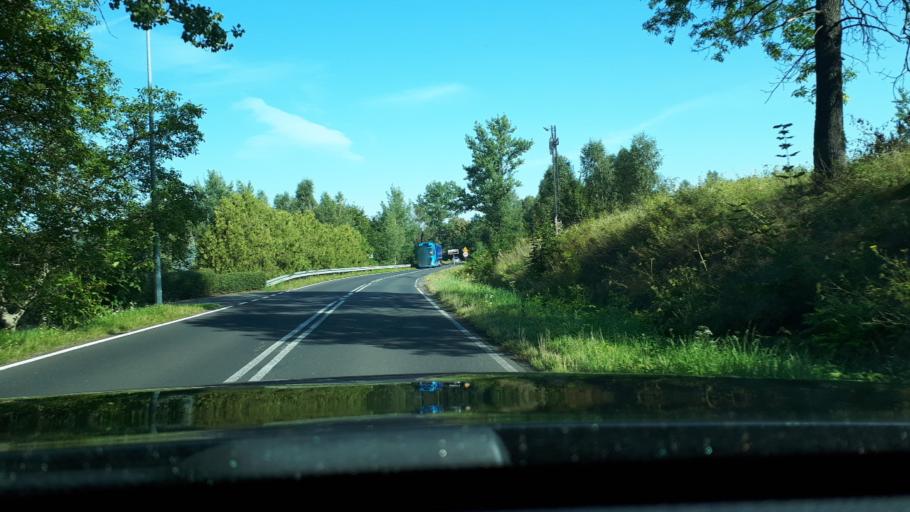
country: PL
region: Lower Silesian Voivodeship
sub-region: Powiat lubanski
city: Lesna
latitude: 51.0411
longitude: 15.2635
